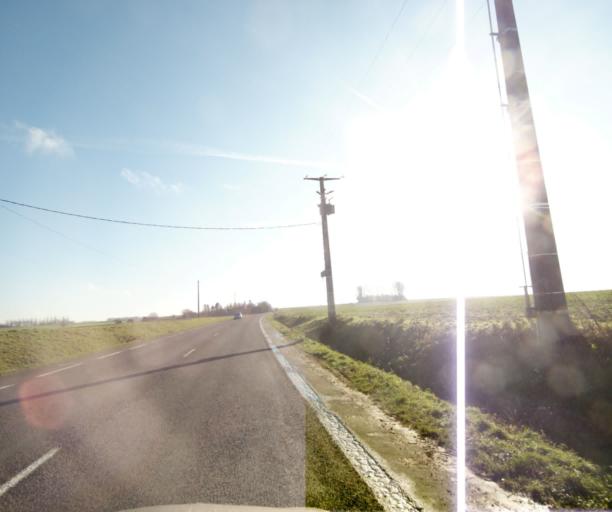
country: FR
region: Nord-Pas-de-Calais
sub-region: Departement du Nord
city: Saultain
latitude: 50.3257
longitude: 3.5620
